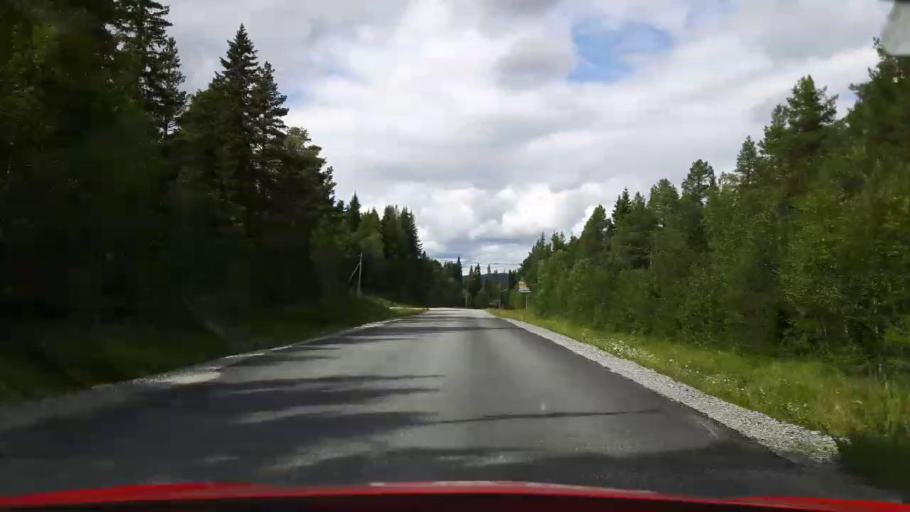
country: NO
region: Hedmark
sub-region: Engerdal
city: Engerdal
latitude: 62.4270
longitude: 12.6841
